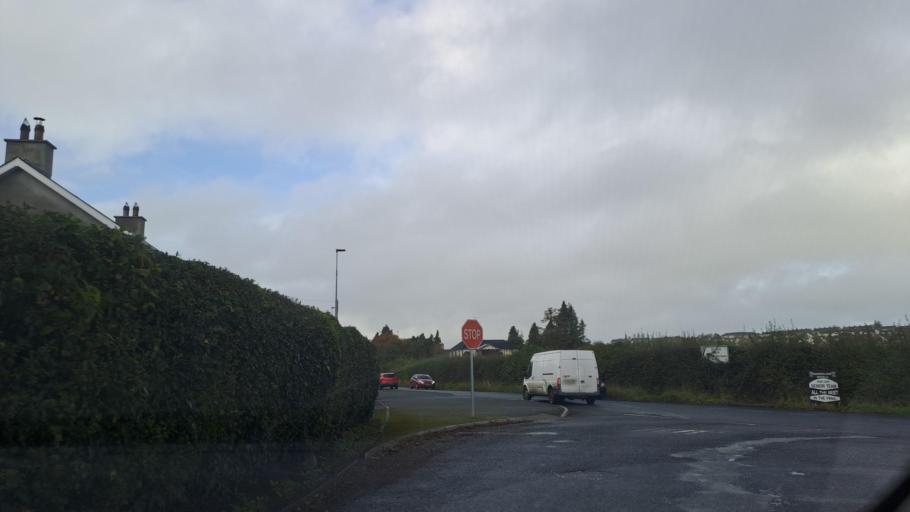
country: IE
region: Ulster
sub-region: County Monaghan
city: Carrickmacross
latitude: 53.9650
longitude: -6.7122
